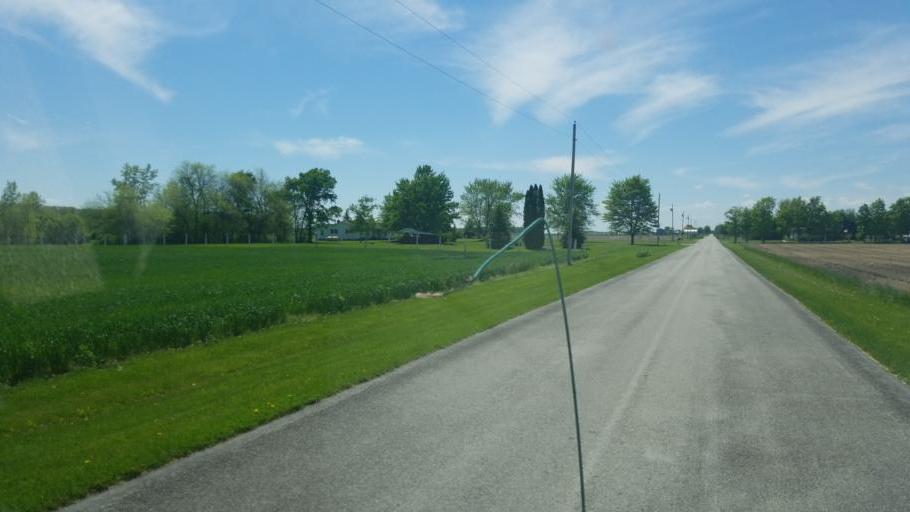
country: US
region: Ohio
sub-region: Huron County
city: Willard
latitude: 41.0703
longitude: -82.8021
